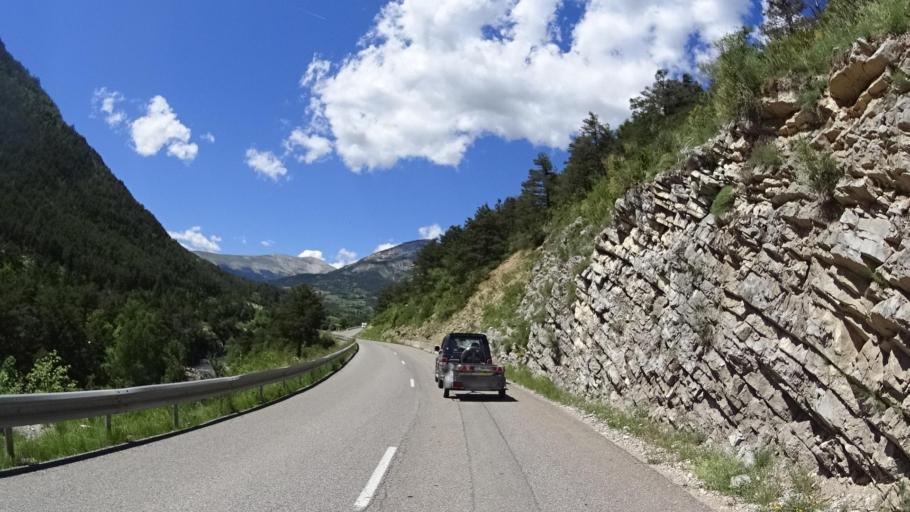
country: FR
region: Provence-Alpes-Cote d'Azur
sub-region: Departement des Alpes-de-Haute-Provence
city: Annot
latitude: 44.0741
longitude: 6.5725
